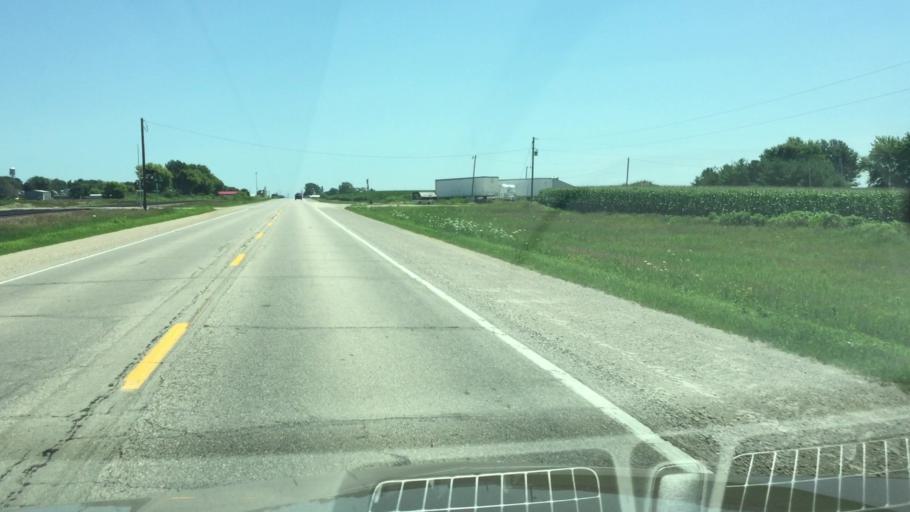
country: US
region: Iowa
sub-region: Cedar County
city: Mechanicsville
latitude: 41.9060
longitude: -91.2702
